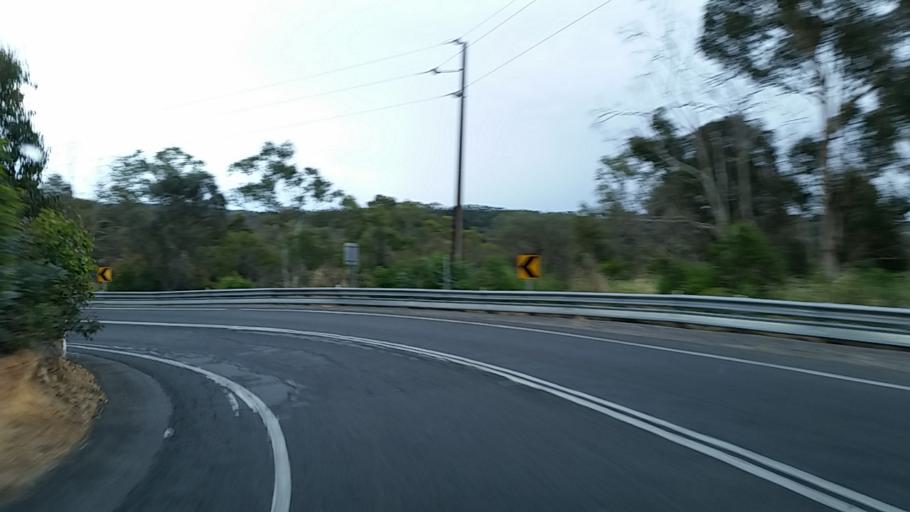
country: AU
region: South Australia
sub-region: Adelaide Hills
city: Gumeracha
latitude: -34.8217
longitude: 138.8343
